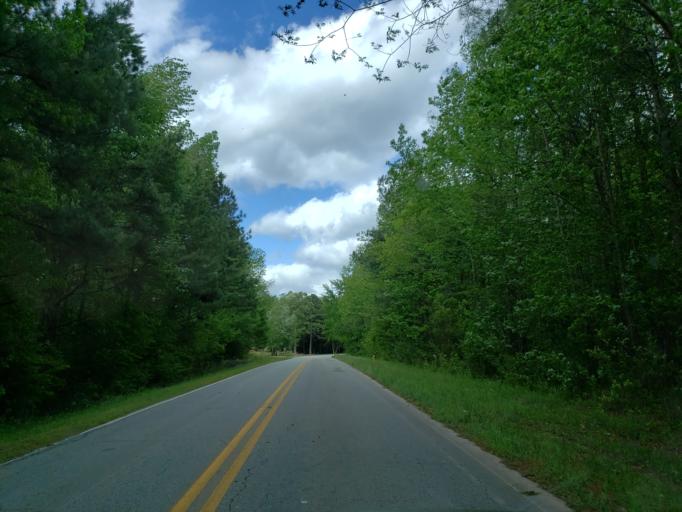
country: US
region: Georgia
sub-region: Haralson County
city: Tallapoosa
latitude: 33.7301
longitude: -85.3177
